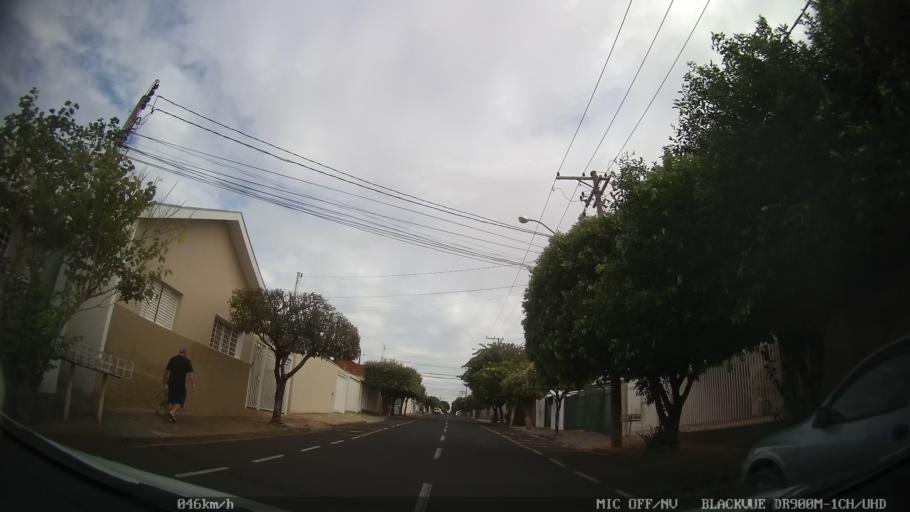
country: BR
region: Sao Paulo
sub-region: Sao Jose Do Rio Preto
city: Sao Jose do Rio Preto
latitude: -20.8151
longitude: -49.3689
